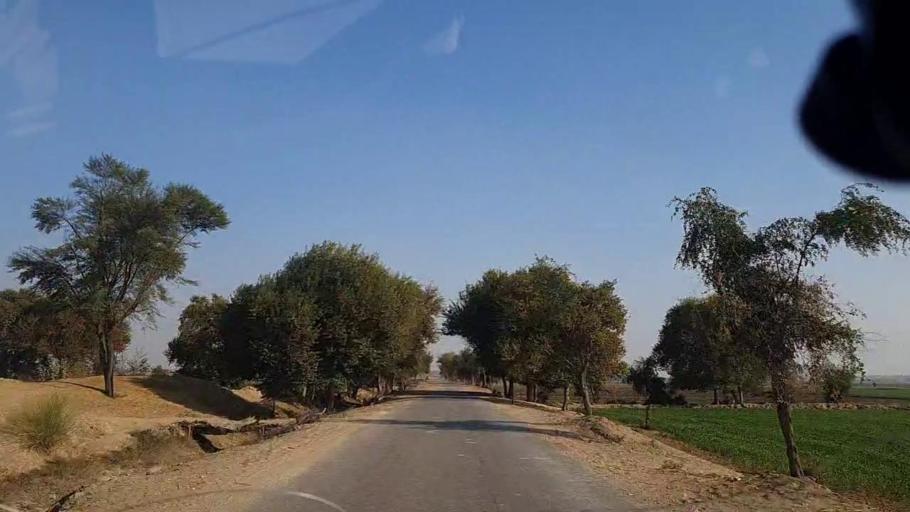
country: PK
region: Sindh
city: Khanpur
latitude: 27.6801
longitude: 69.5580
